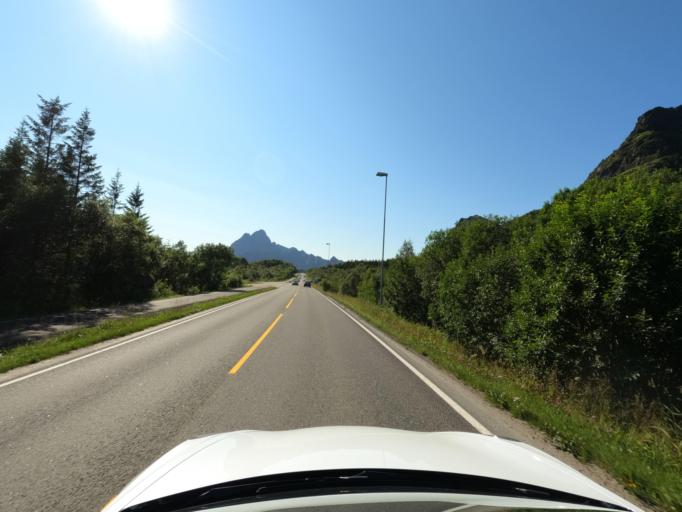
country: NO
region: Nordland
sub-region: Vagan
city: Kabelvag
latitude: 68.2154
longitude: 14.4335
